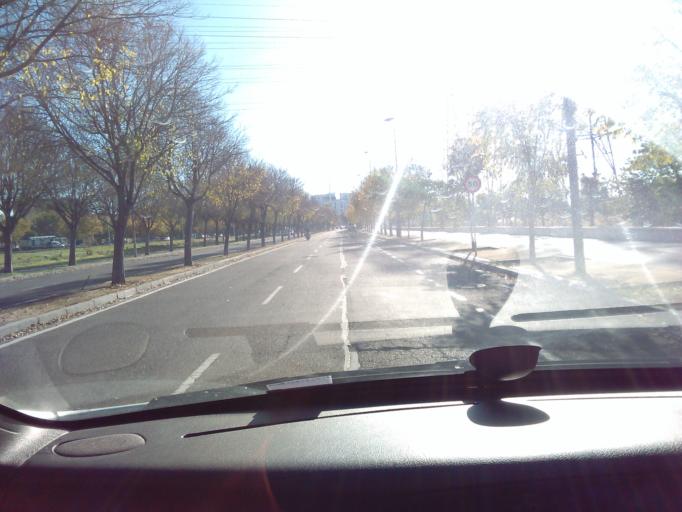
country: ES
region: Andalusia
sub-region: Provincia de Sevilla
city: Sevilla
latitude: 37.4168
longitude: -5.9875
